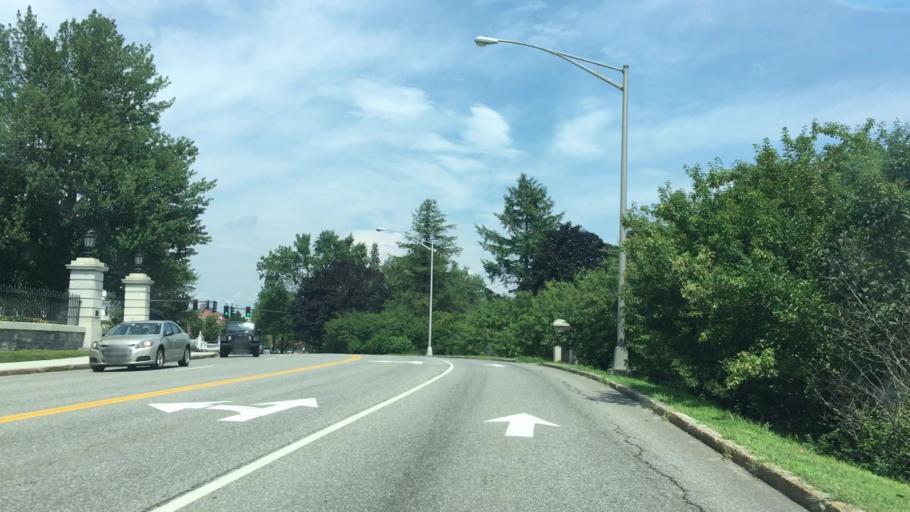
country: US
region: Maine
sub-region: Kennebec County
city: Augusta
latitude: 44.3067
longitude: -69.7808
